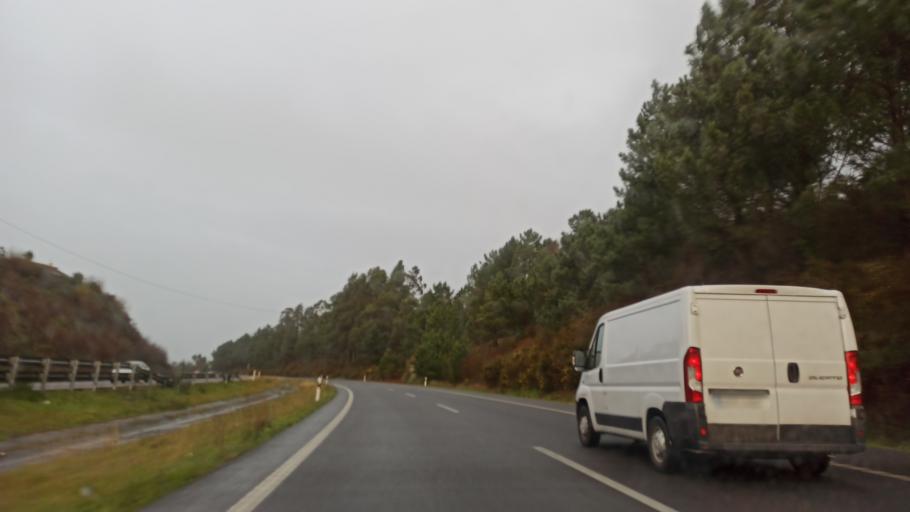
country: ES
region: Galicia
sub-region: Provincia da Coruna
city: Cambre
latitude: 43.2622
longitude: -8.3359
